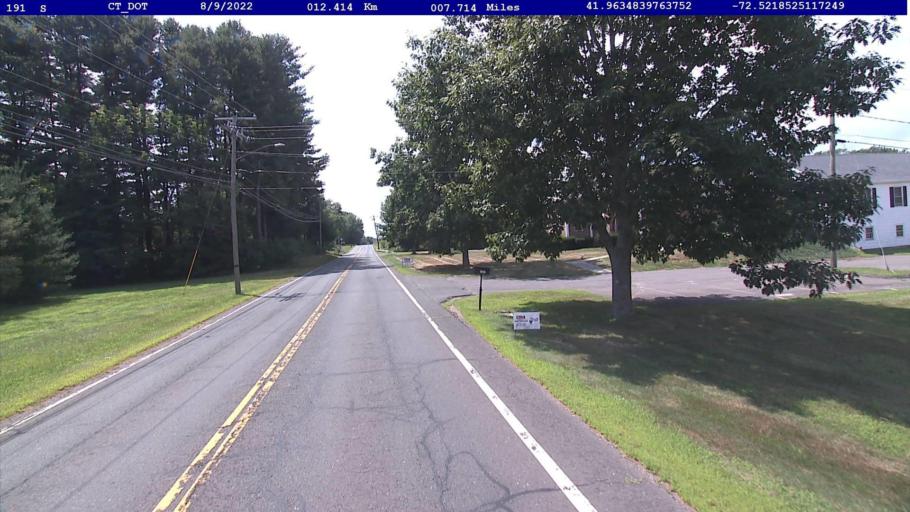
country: US
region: Connecticut
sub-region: Hartford County
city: Hazardville
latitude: 41.9635
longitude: -72.5204
